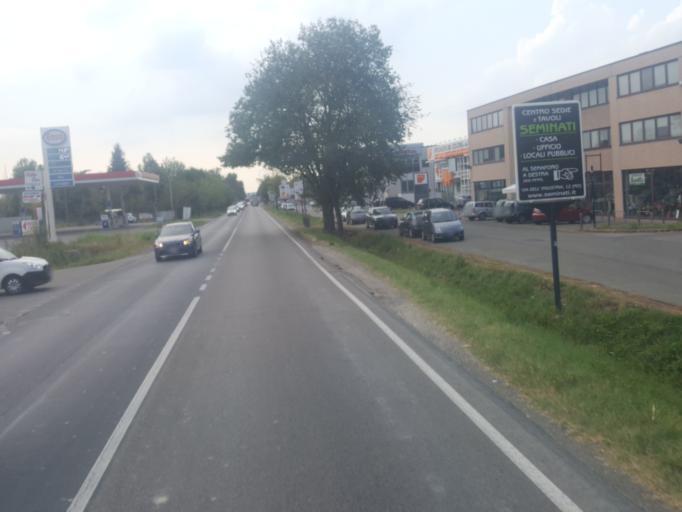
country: IT
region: Emilia-Romagna
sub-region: Provincia di Modena
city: San Damaso
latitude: 44.6263
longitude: 10.9741
